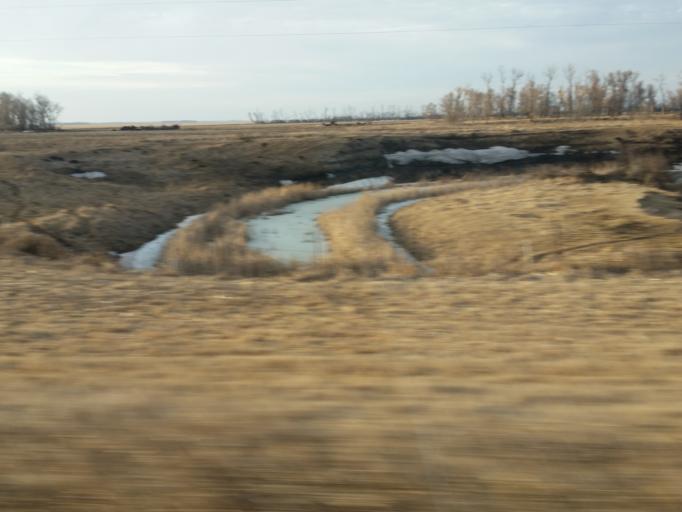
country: US
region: North Dakota
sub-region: Traill County
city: Mayville
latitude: 47.3531
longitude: -97.3023
